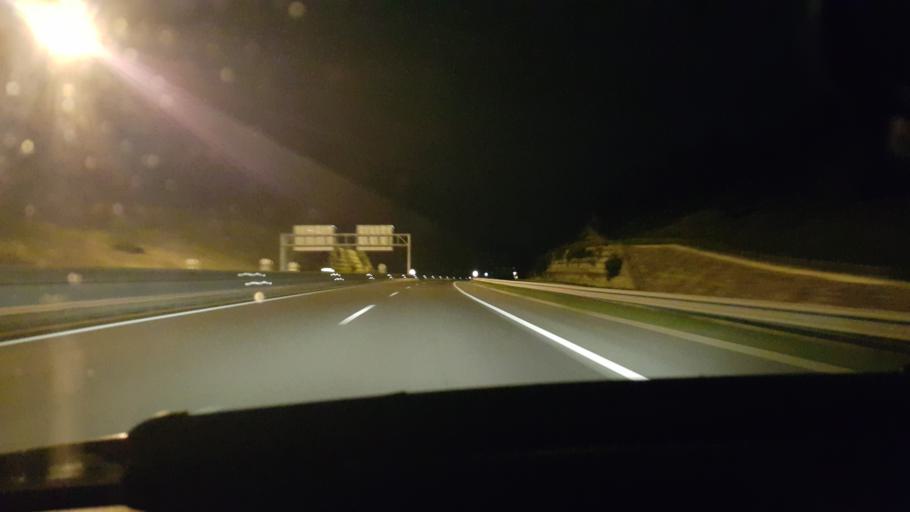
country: SI
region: Pesnica
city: Pesnica pri Mariboru
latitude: 46.5840
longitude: 15.6888
